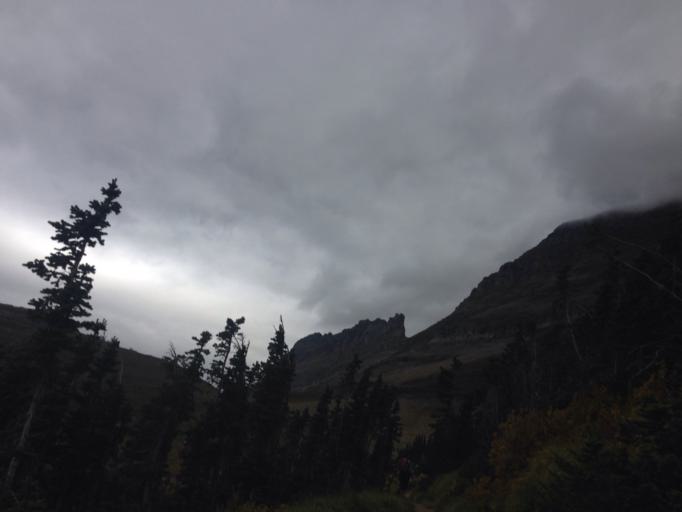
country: US
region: Montana
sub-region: Flathead County
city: Columbia Falls
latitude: 48.7301
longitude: -113.7195
